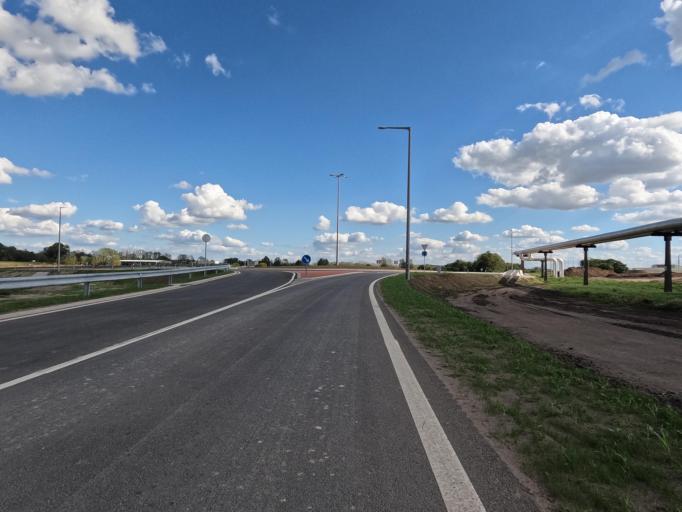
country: HU
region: Tolna
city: Paks
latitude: 46.5999
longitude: 18.8496
